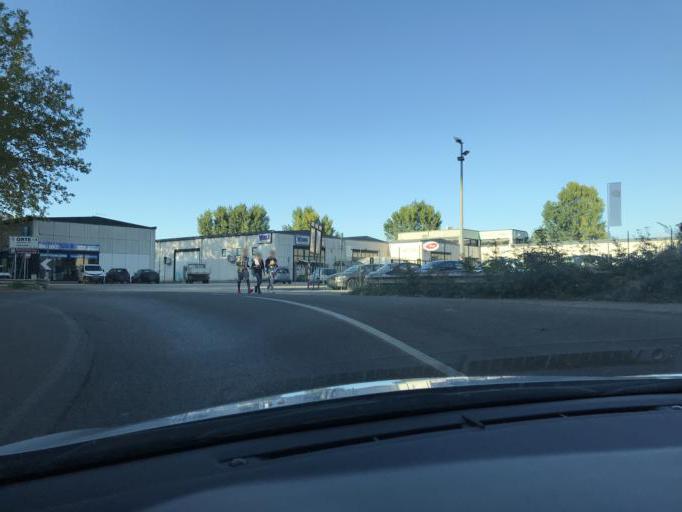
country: IT
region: Latium
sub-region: Provincia di Viterbo
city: Orte
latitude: 42.4516
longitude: 12.3885
